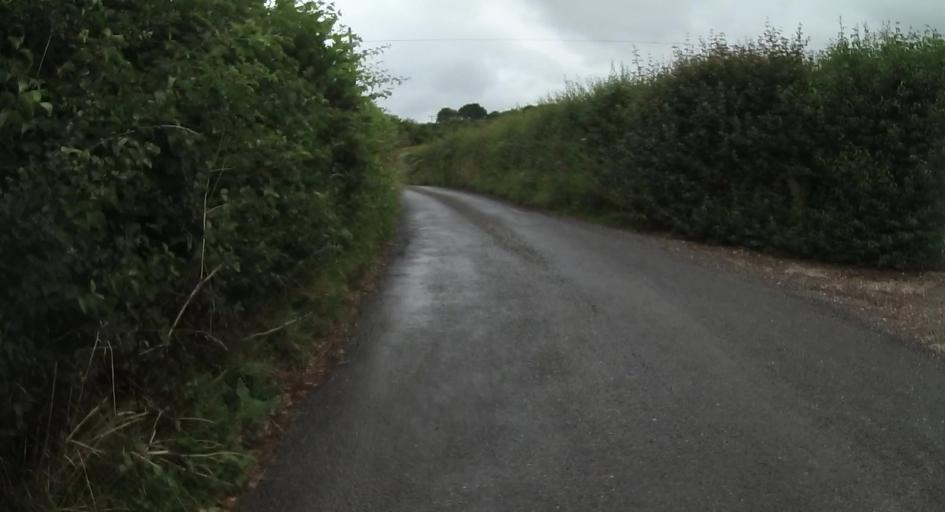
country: GB
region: England
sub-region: Hampshire
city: Long Sutton
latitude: 51.1961
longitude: -0.9135
